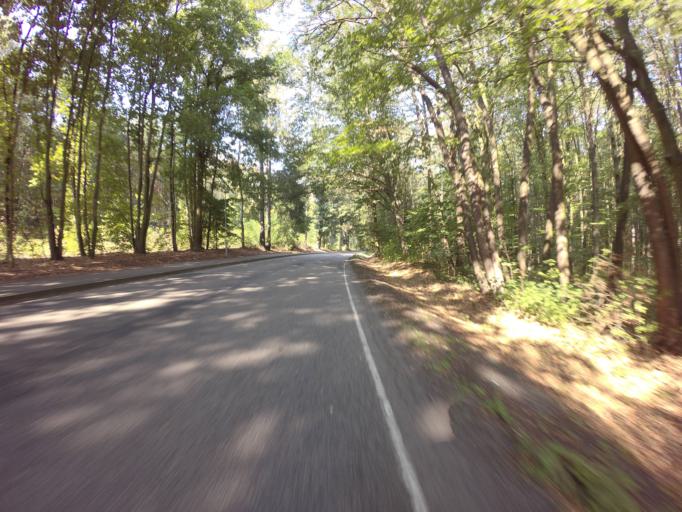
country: CZ
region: Central Bohemia
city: Tynec nad Sazavou
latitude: 49.8270
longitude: 14.6060
